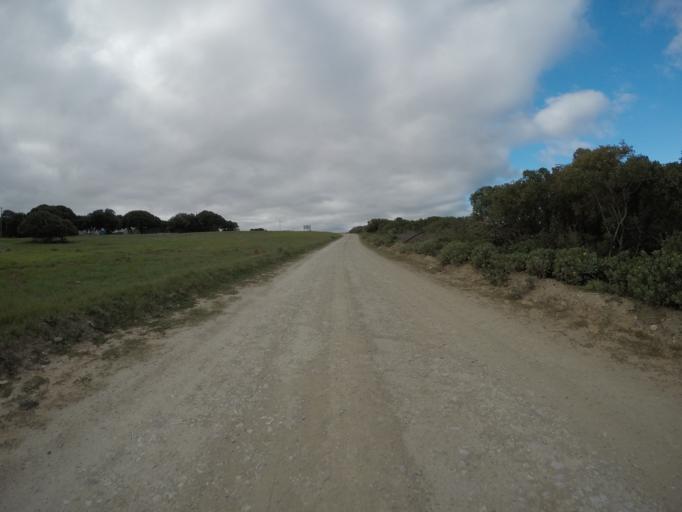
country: ZA
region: Western Cape
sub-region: Eden District Municipality
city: Riversdale
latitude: -34.4219
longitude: 21.3311
